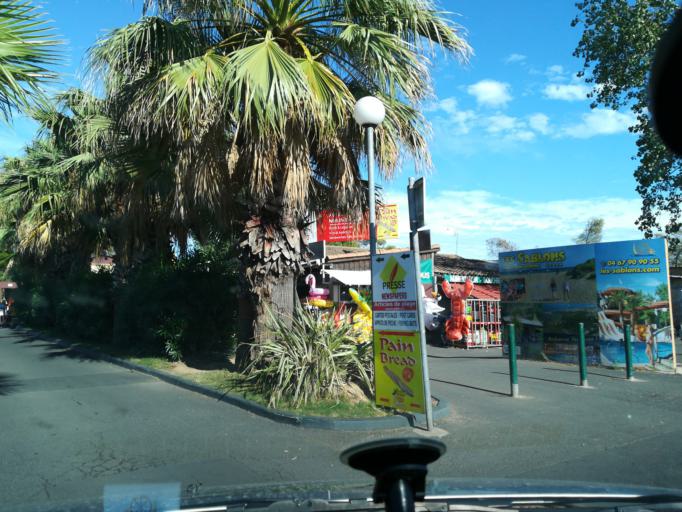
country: FR
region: Languedoc-Roussillon
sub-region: Departement de l'Herault
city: Portiragnes
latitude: 43.2800
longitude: 3.3637
